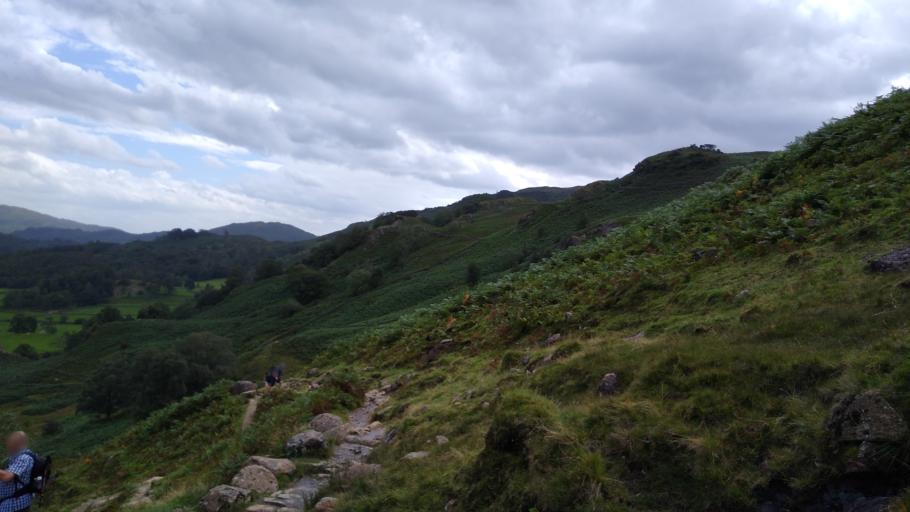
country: GB
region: England
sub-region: Cumbria
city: Ambleside
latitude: 54.4697
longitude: -3.0545
